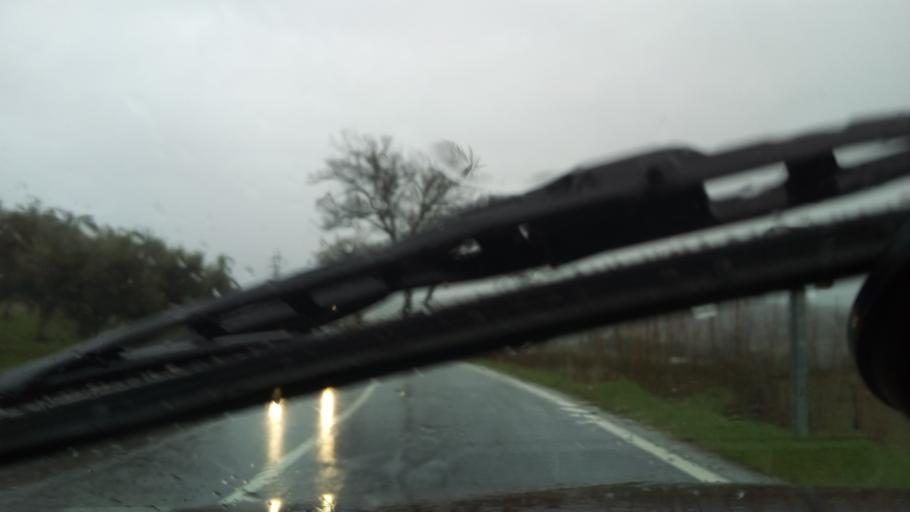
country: PT
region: Guarda
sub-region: Fornos de Algodres
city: Fornos de Algodres
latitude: 40.5409
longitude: -7.5362
